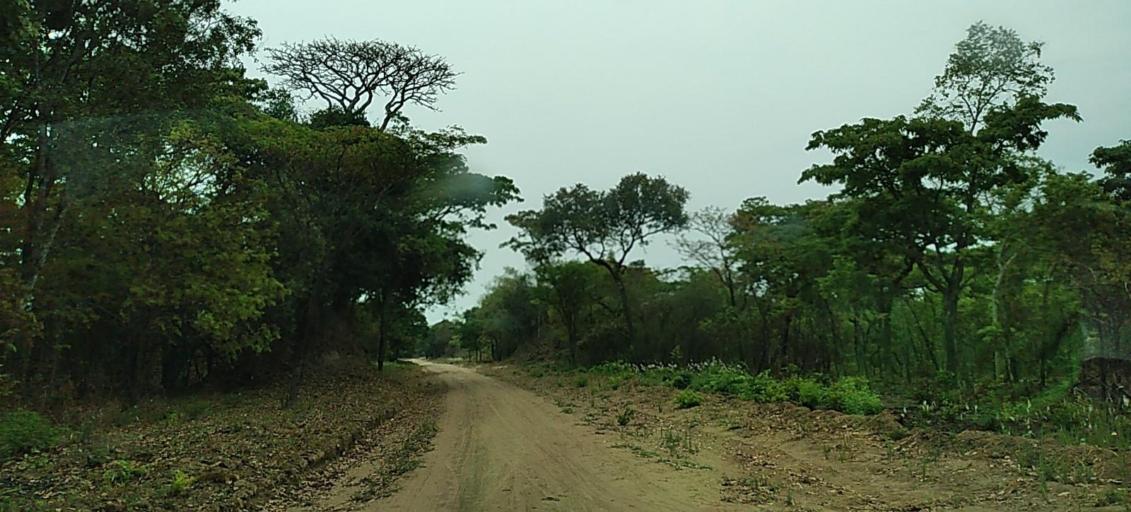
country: ZM
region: North-Western
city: Solwezi
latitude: -12.5287
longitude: 26.5230
